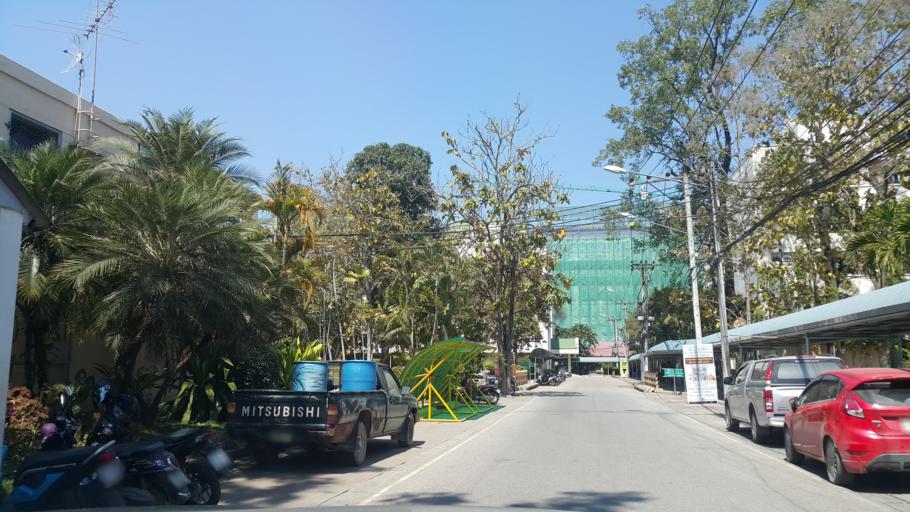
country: TH
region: Chiang Mai
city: San Sai
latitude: 18.8988
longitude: 99.0093
